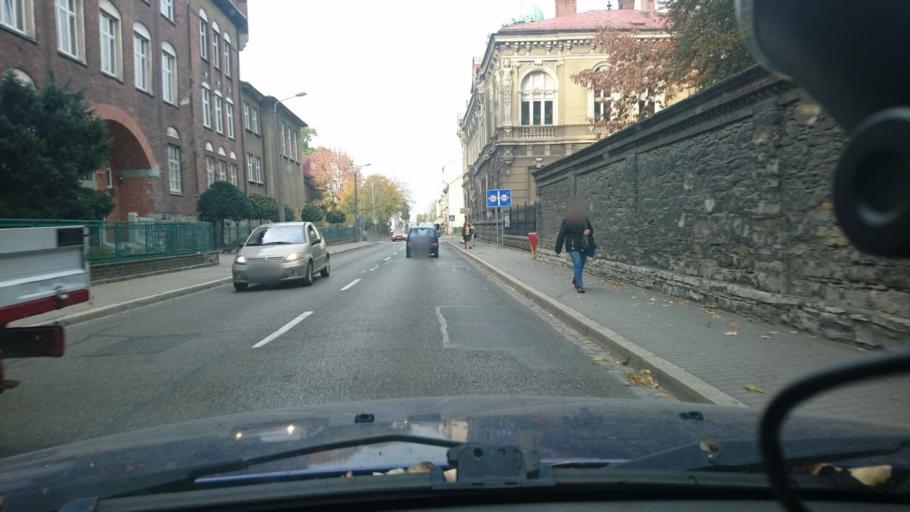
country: PL
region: Silesian Voivodeship
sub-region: Bielsko-Biala
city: Bielsko-Biala
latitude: 49.8269
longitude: 19.0530
